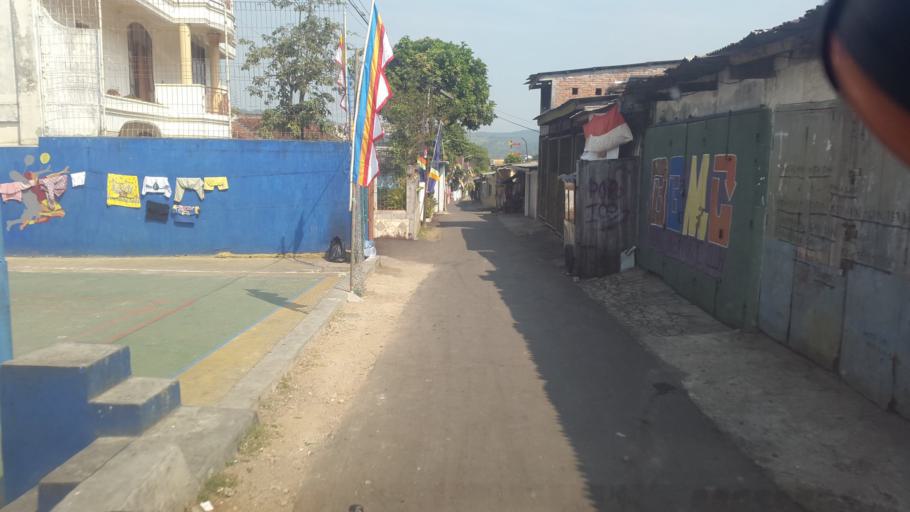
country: ID
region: West Java
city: Gunungkalong
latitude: -6.8910
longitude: 106.7848
